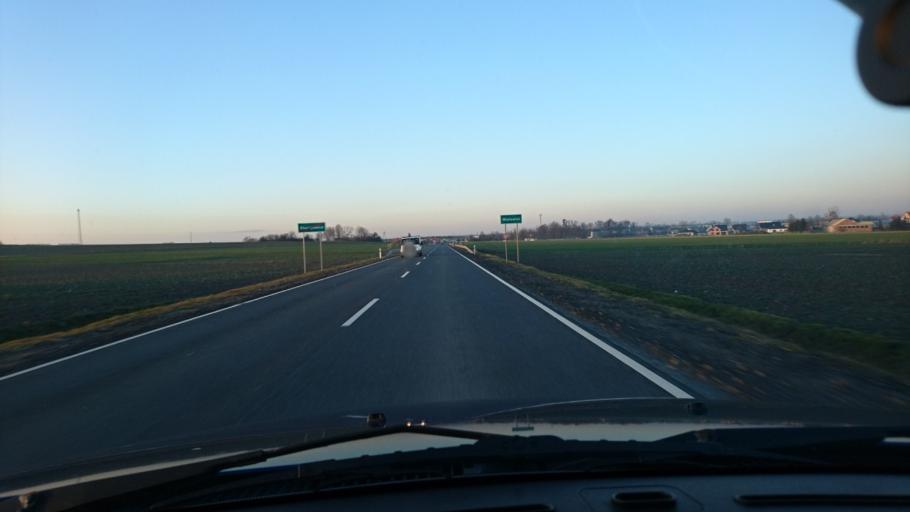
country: PL
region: Silesian Voivodeship
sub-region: Powiat gliwicki
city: Wielowies
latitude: 50.4981
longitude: 18.6063
